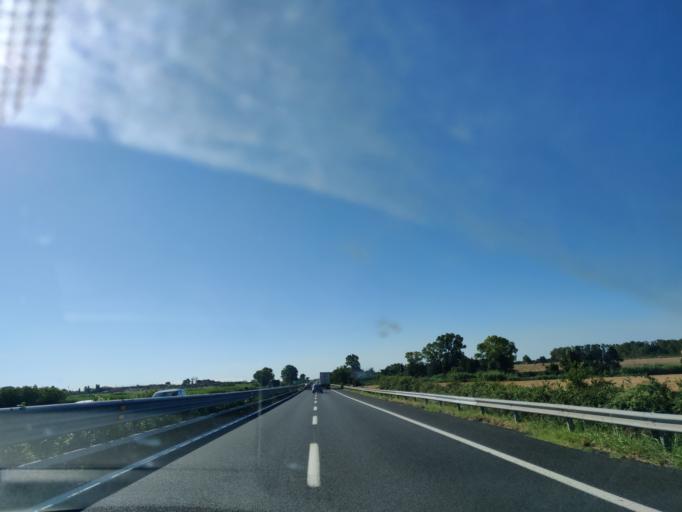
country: IT
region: Latium
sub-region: Citta metropolitana di Roma Capitale
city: Marina di Cerveteri
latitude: 41.9976
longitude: 12.0487
